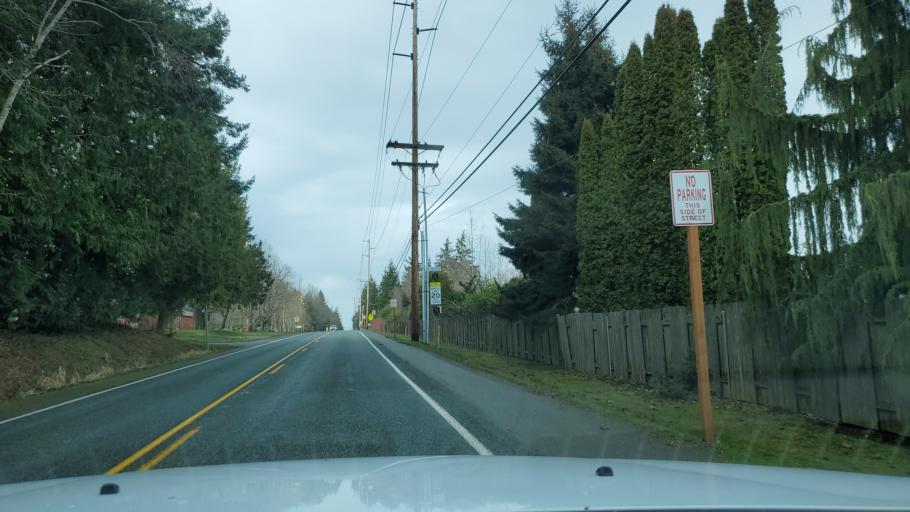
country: US
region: Washington
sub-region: Skagit County
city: Anacortes
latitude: 48.4452
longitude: -122.5816
